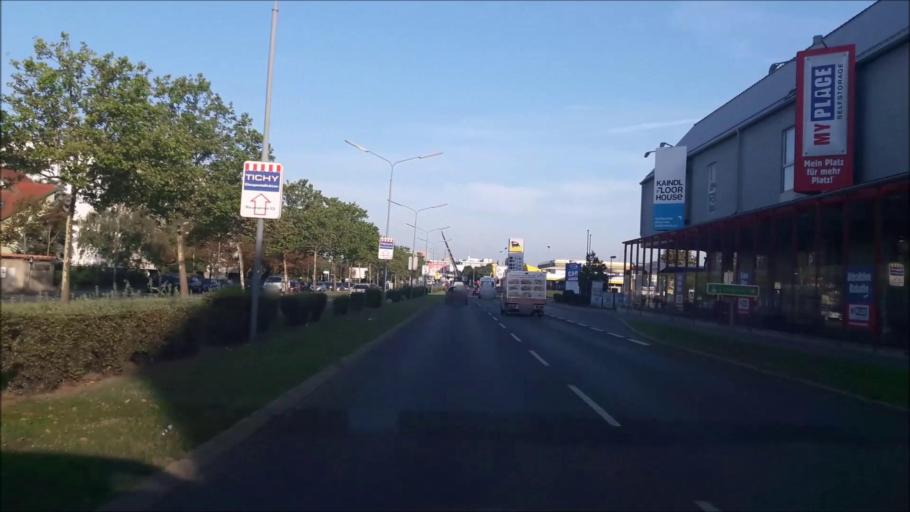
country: AT
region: Vienna
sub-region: Wien Stadt
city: Vienna
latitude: 48.1630
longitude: 16.3783
